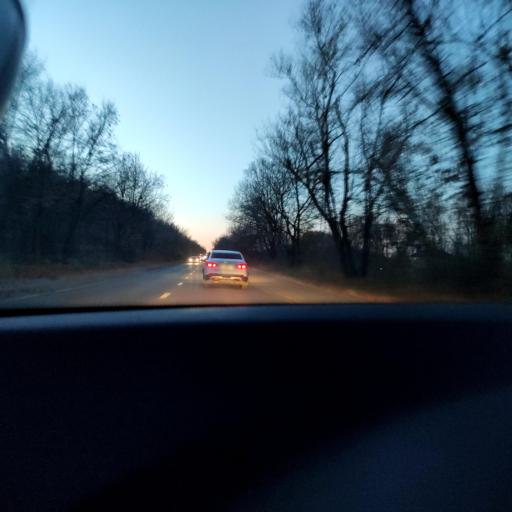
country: RU
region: Samara
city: Petra-Dubrava
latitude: 53.3105
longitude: 50.2756
